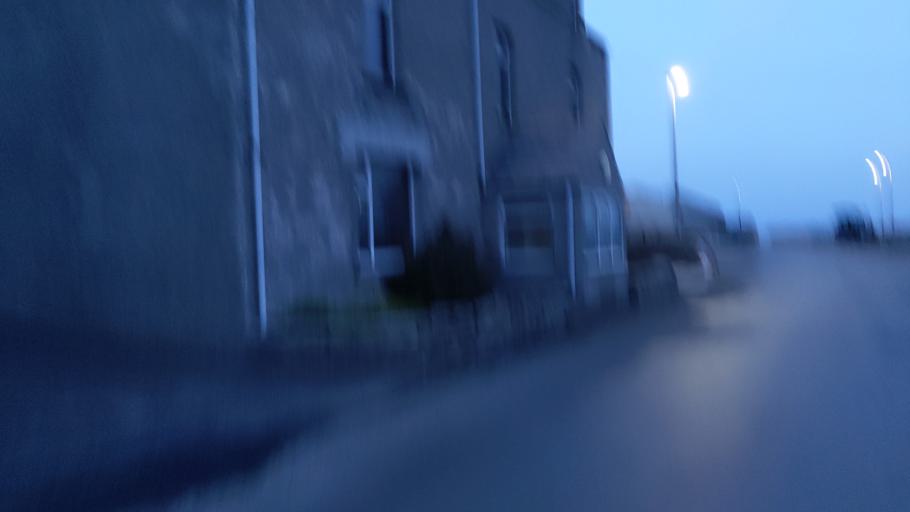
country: GB
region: Scotland
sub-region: Orkney Islands
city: Kirkwall
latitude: 59.3245
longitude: -2.9757
